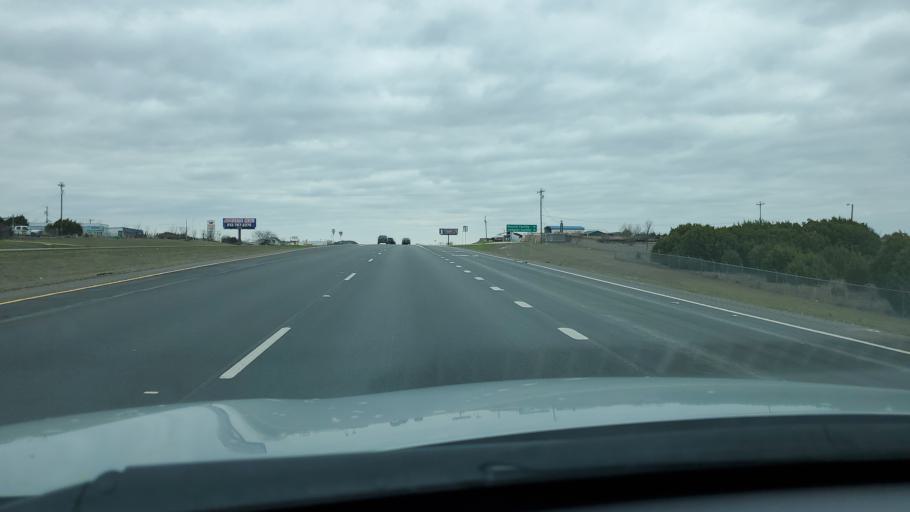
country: US
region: Texas
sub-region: Bell County
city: Killeen
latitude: 31.0143
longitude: -97.7525
